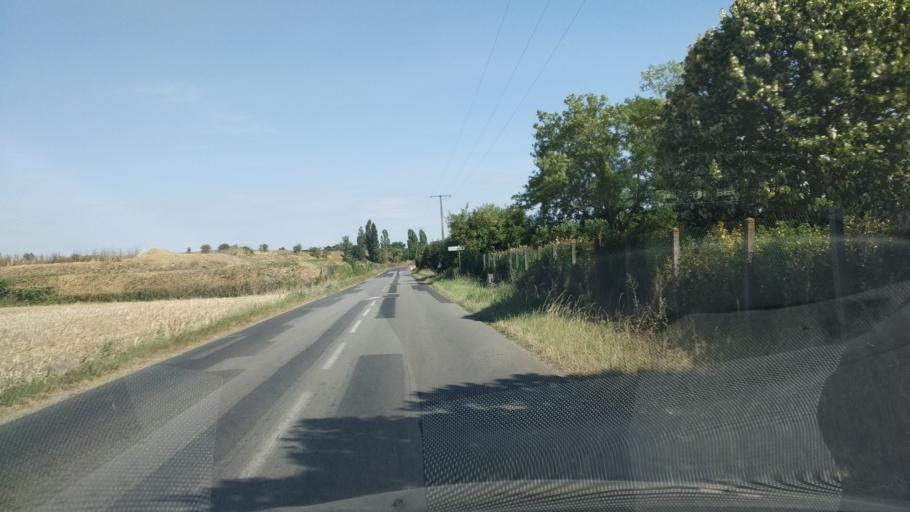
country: FR
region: Poitou-Charentes
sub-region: Departement de la Vienne
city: Cisse
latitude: 46.6629
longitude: 0.2064
